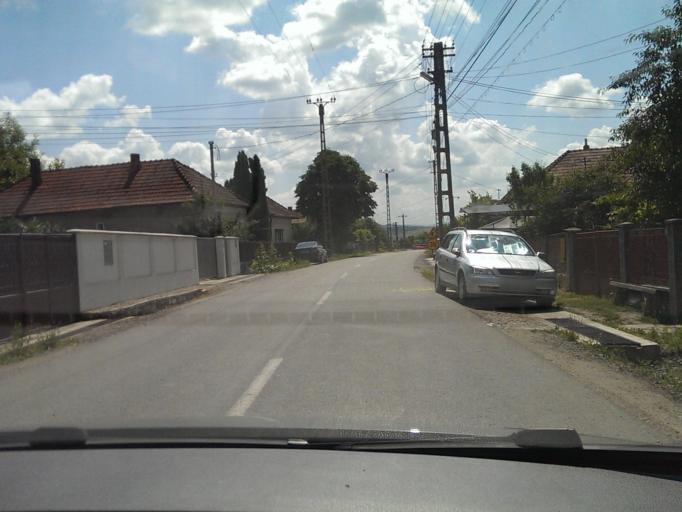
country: RO
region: Cluj
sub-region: Comuna Apahida
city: Sannicoara
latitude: 46.7909
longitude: 23.7205
